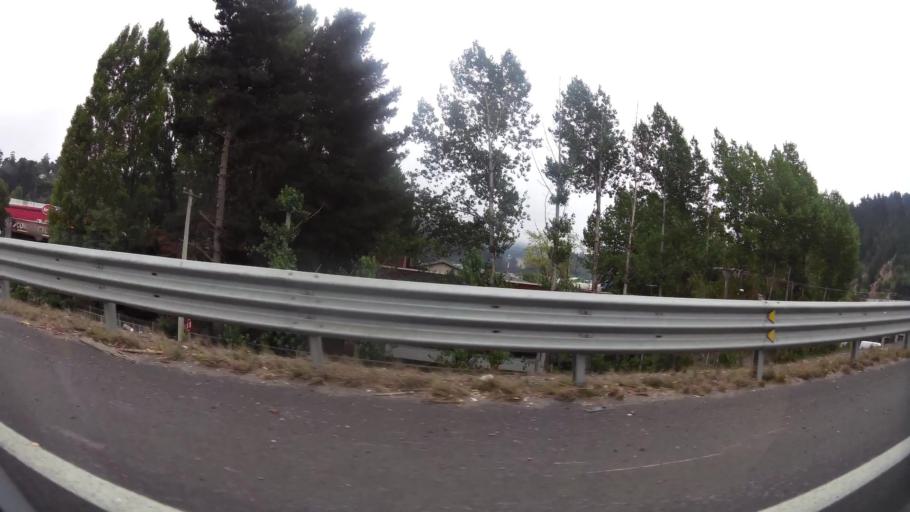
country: CL
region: Biobio
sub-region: Provincia de Concepcion
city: Concepcion
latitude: -36.8209
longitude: -72.9947
